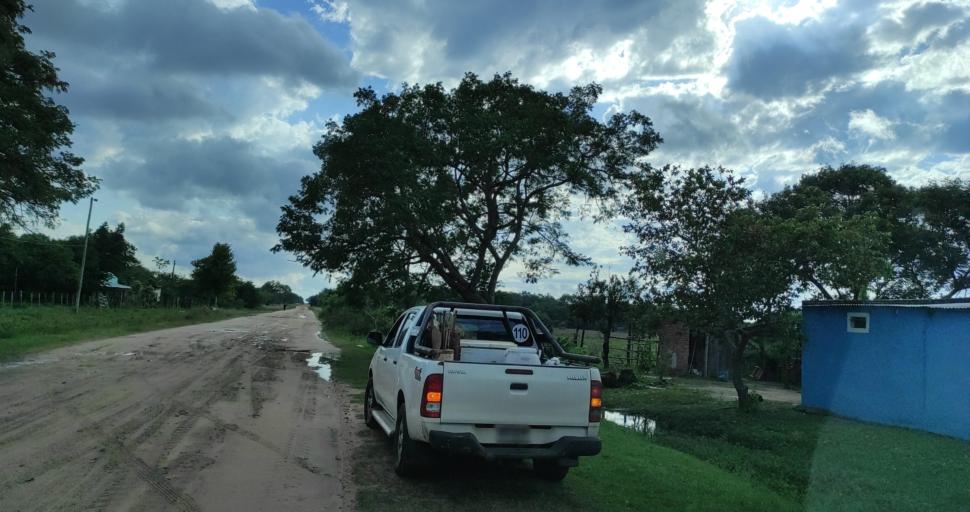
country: AR
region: Corrientes
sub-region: Departamento de San Cosme
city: San Cosme
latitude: -27.3670
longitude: -58.3648
